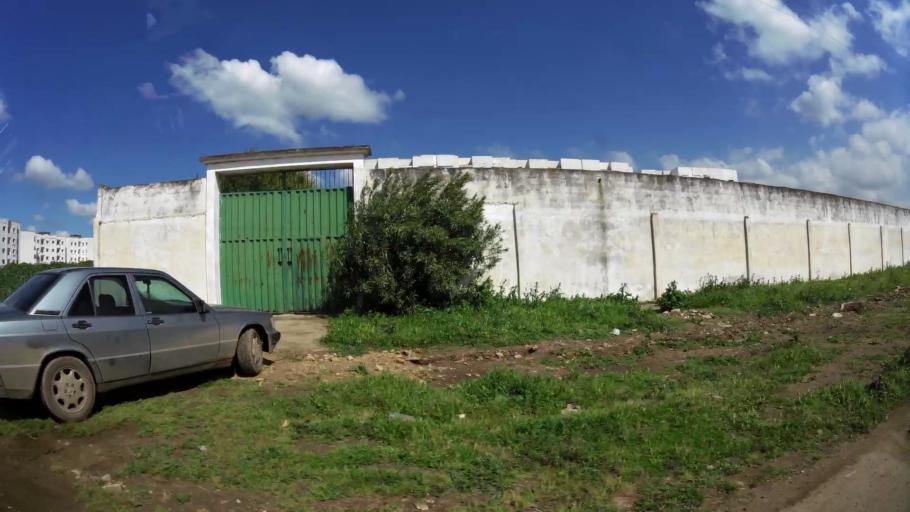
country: MA
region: Grand Casablanca
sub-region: Mediouna
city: Mediouna
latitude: 33.4423
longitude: -7.5200
